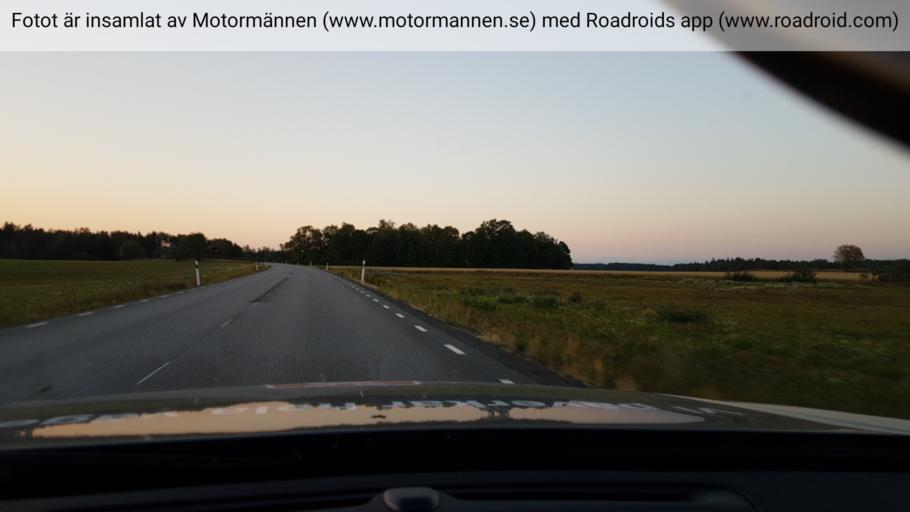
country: SE
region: Uppsala
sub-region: Heby Kommun
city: OEstervala
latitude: 60.1164
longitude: 17.2172
